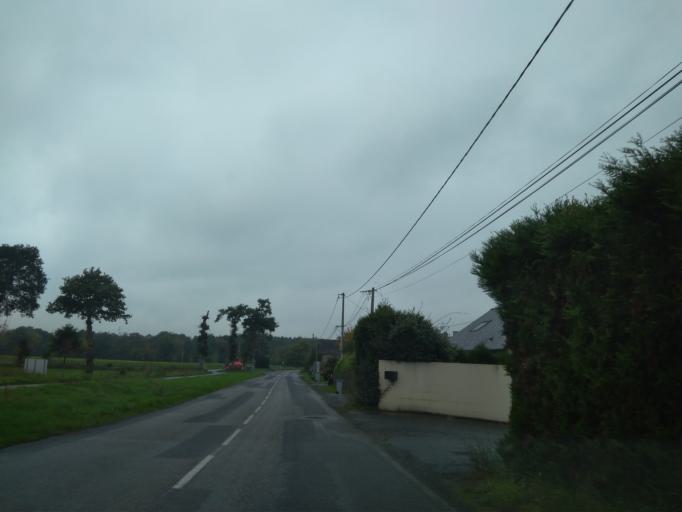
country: FR
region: Brittany
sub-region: Departement d'Ille-et-Vilaine
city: Saint-Gregoire
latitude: 48.1490
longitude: -1.6726
